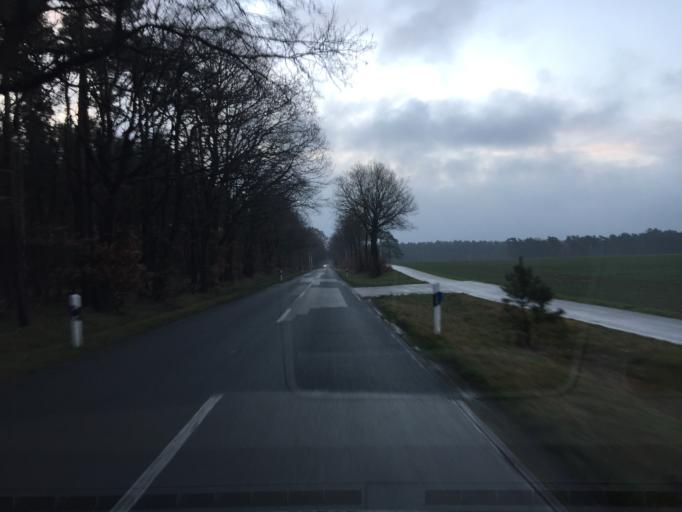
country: DE
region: Lower Saxony
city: Liebenau
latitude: 52.6207
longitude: 9.0624
